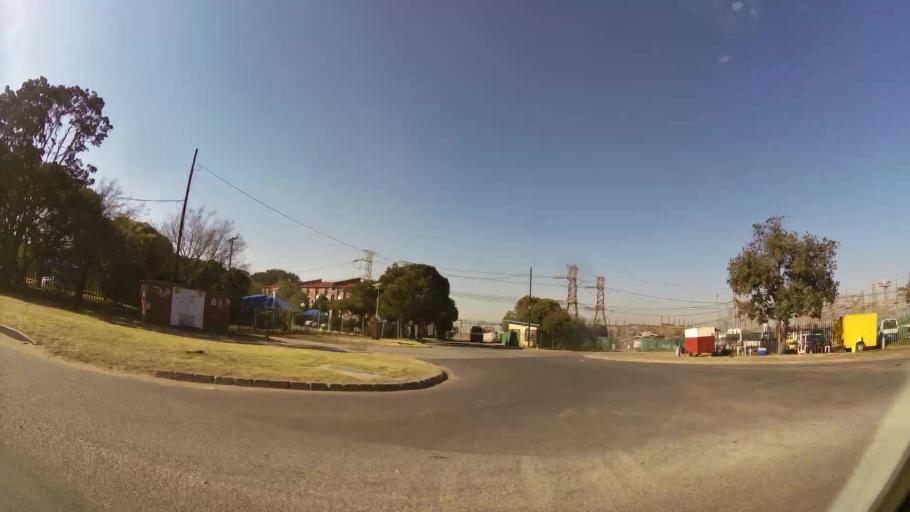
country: ZA
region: Gauteng
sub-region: Ekurhuleni Metropolitan Municipality
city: Germiston
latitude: -26.2276
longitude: 28.1149
